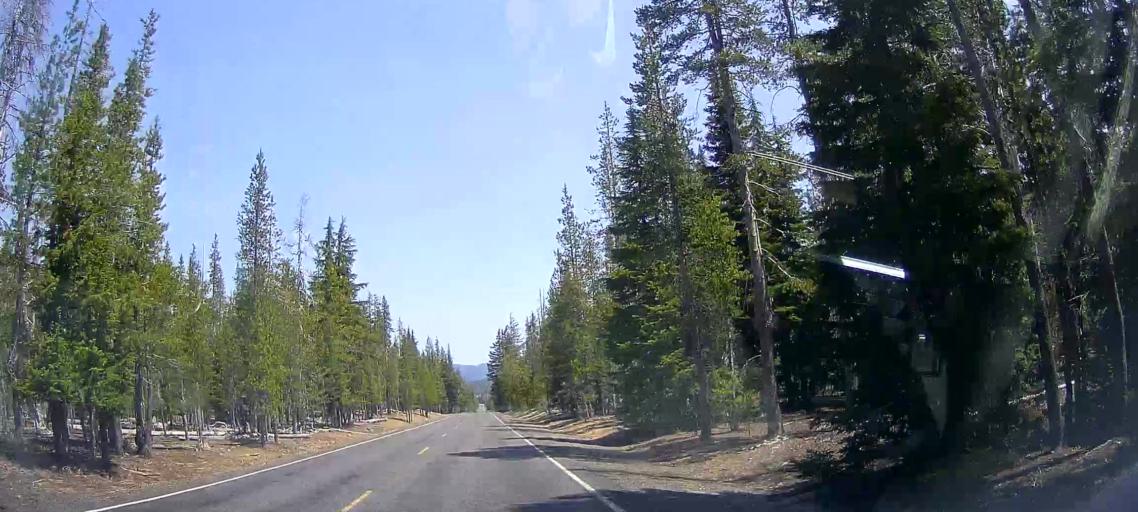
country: US
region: Oregon
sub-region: Jackson County
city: Shady Cove
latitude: 43.0124
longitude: -122.1291
